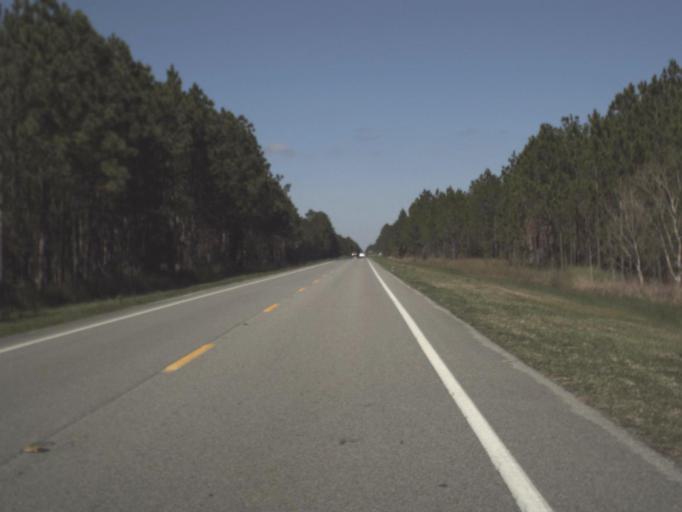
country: US
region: Florida
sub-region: Gulf County
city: Port Saint Joe
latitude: 29.9025
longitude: -85.2096
